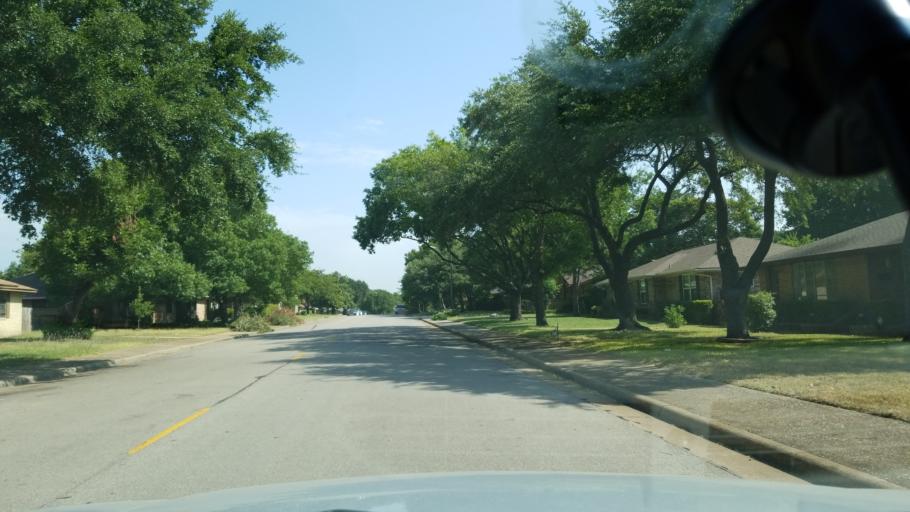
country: US
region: Texas
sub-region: Dallas County
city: Duncanville
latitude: 32.6809
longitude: -96.8481
